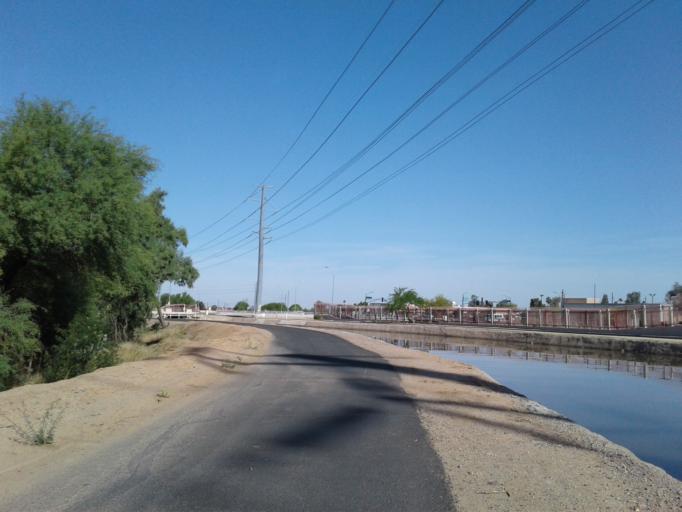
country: US
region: Arizona
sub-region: Maricopa County
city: Glendale
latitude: 33.5951
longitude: -112.1672
